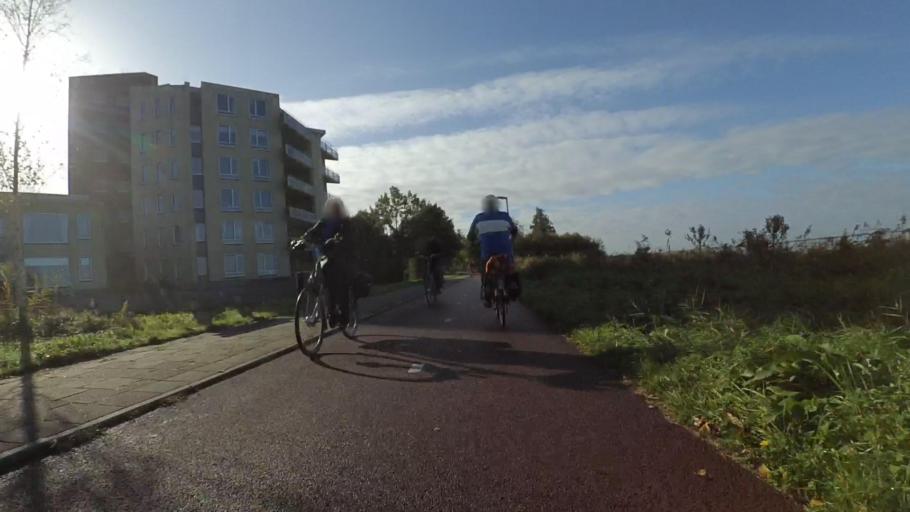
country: NL
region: Gelderland
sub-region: Gemeente Harderwijk
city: Harderwijk
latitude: 52.3460
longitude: 5.6121
